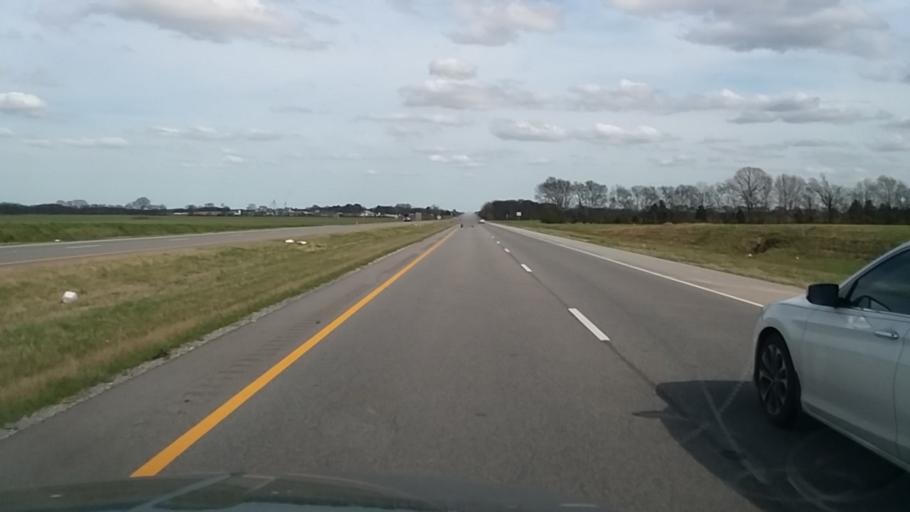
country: US
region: Alabama
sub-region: Colbert County
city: Muscle Shoals
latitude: 34.6851
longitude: -87.5851
